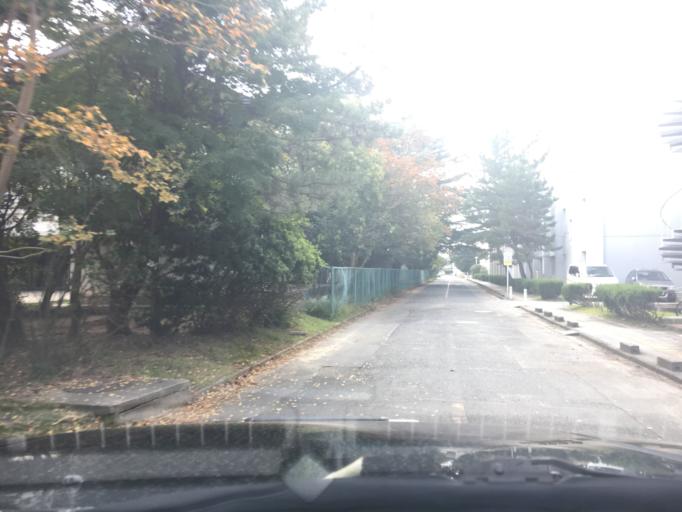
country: JP
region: Nara
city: Nara-shi
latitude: 34.6753
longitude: 135.8430
